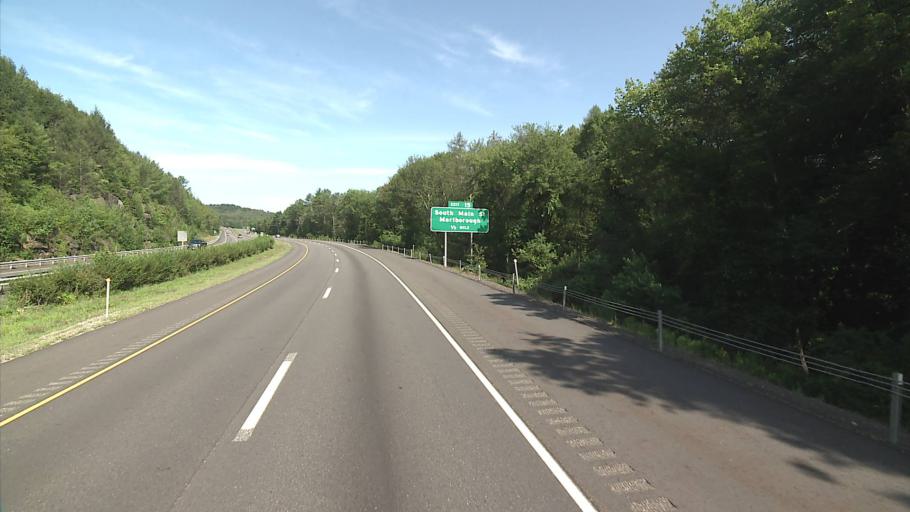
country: US
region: Connecticut
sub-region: Hartford County
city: Terramuggus
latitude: 41.6038
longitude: -72.4210
